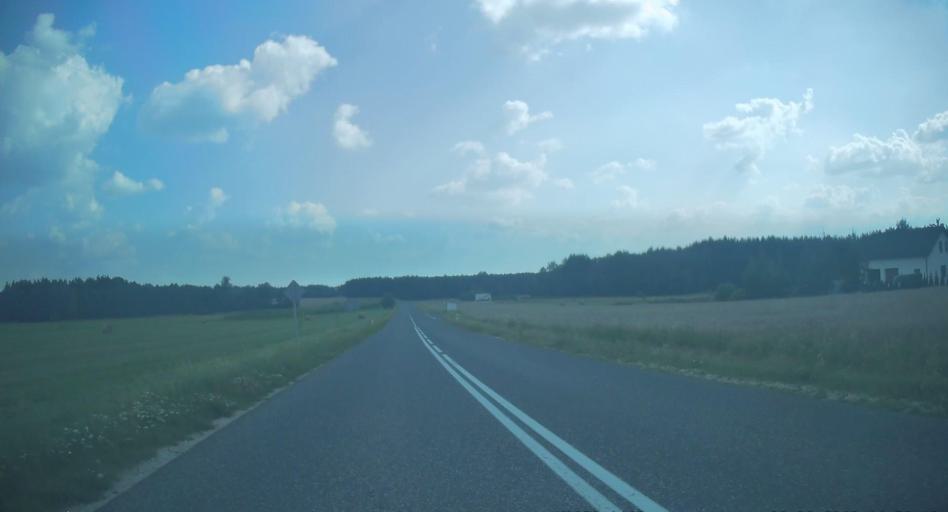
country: PL
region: Swietokrzyskie
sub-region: Powiat kielecki
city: Lopuszno
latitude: 50.9053
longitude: 20.2470
